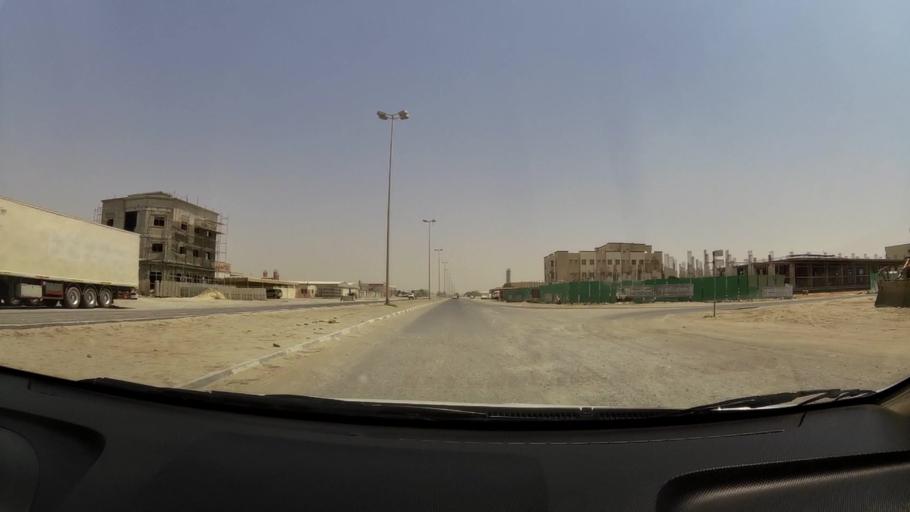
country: AE
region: Umm al Qaywayn
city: Umm al Qaywayn
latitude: 25.5104
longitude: 55.5583
